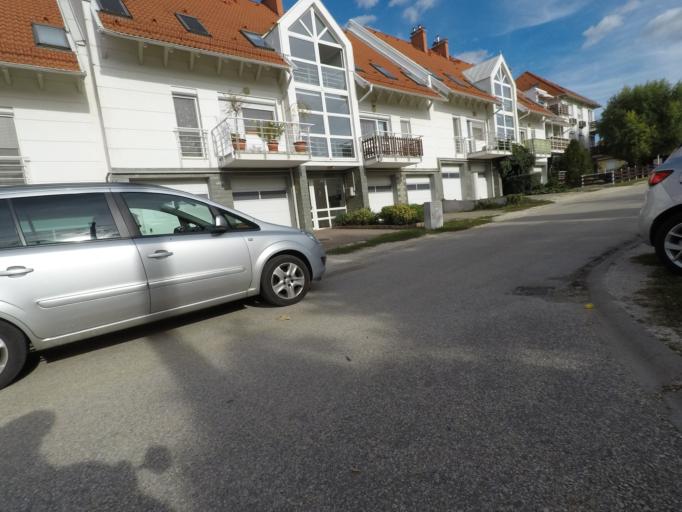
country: HU
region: Pest
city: Pomaz
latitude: 47.6445
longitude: 19.0237
